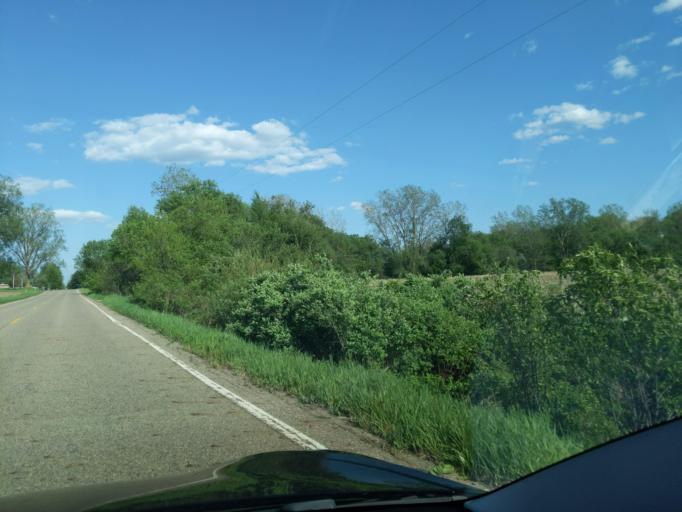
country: US
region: Michigan
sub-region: Eaton County
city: Dimondale
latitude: 42.6828
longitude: -84.6992
